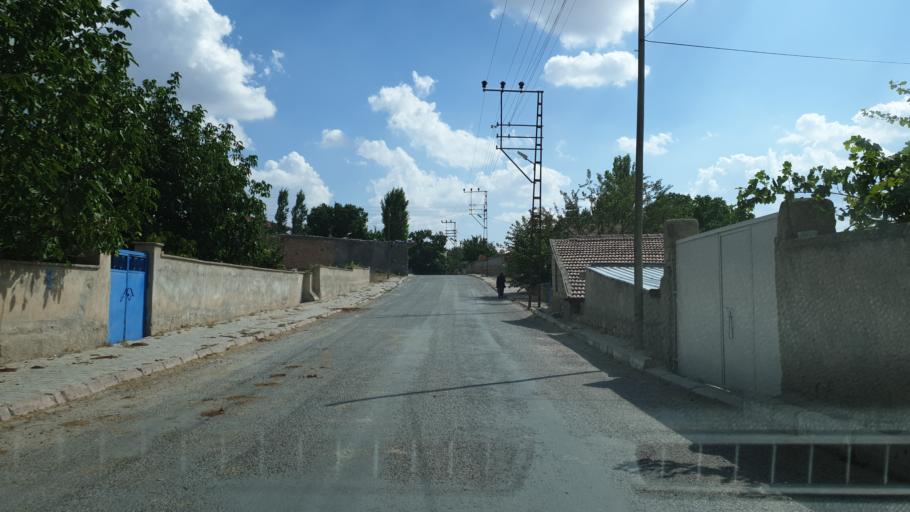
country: TR
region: Kayseri
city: Felahiye
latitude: 39.0912
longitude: 35.5631
